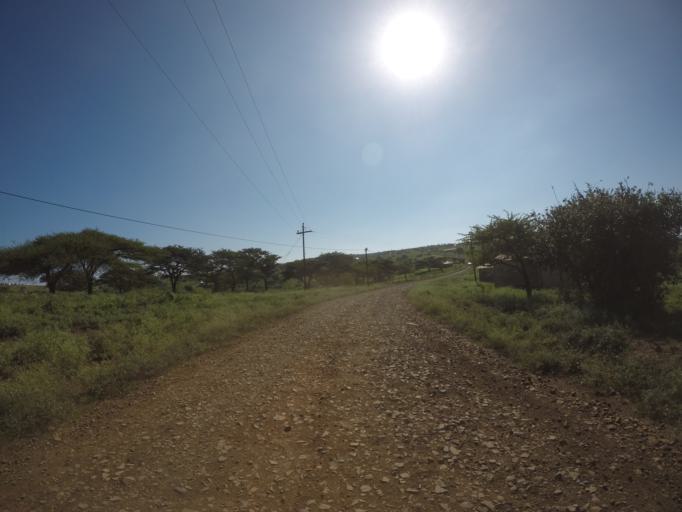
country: ZA
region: KwaZulu-Natal
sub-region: uThungulu District Municipality
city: Empangeni
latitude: -28.5723
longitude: 31.7240
